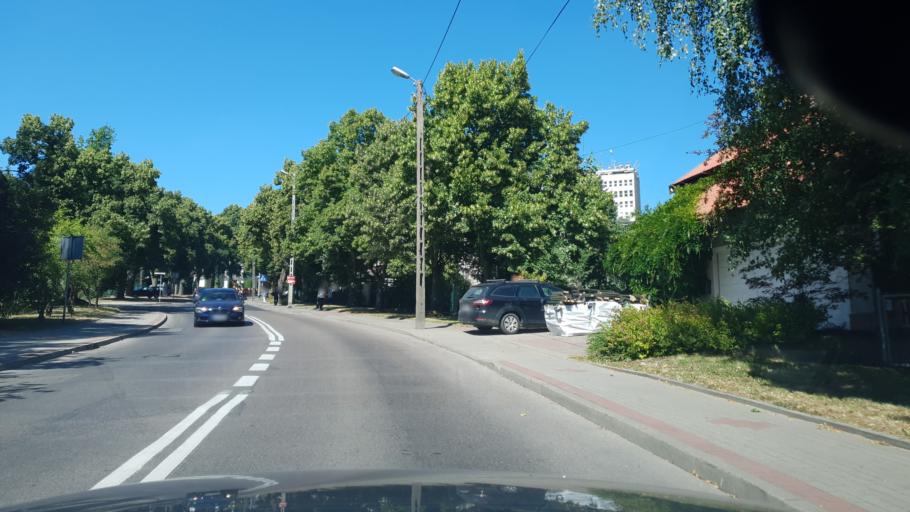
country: PL
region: Pomeranian Voivodeship
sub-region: Gdynia
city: Gdynia
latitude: 54.4861
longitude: 18.5467
